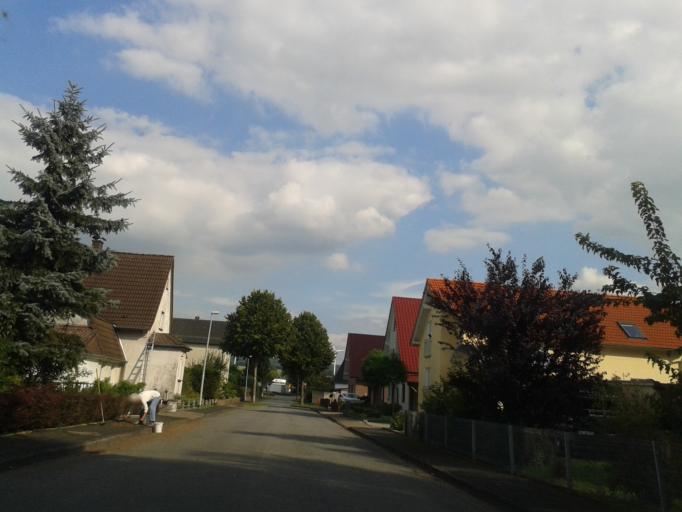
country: DE
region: North Rhine-Westphalia
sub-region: Regierungsbezirk Detmold
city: Schlangen
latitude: 51.7994
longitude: 8.8339
